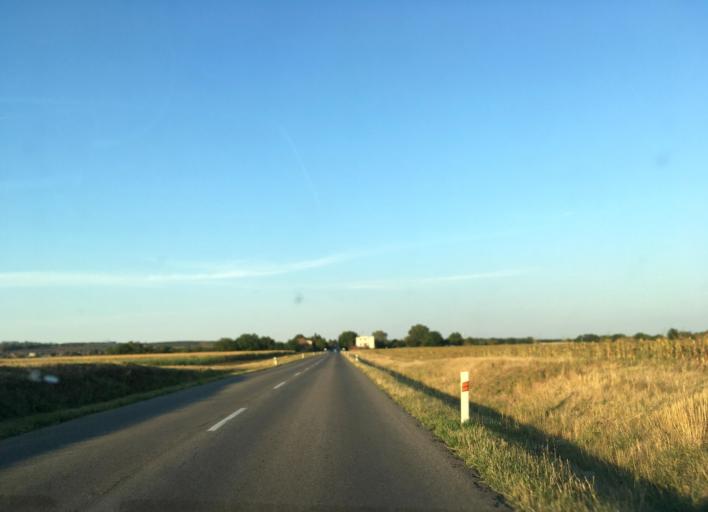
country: HU
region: Komarom-Esztergom
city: Dunaalmas
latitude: 47.7982
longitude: 18.3103
